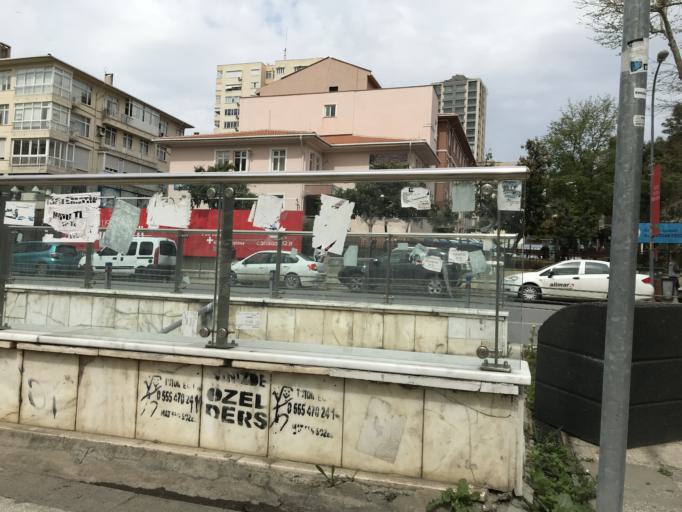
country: TR
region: Istanbul
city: UEskuedar
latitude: 40.9727
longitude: 29.0574
